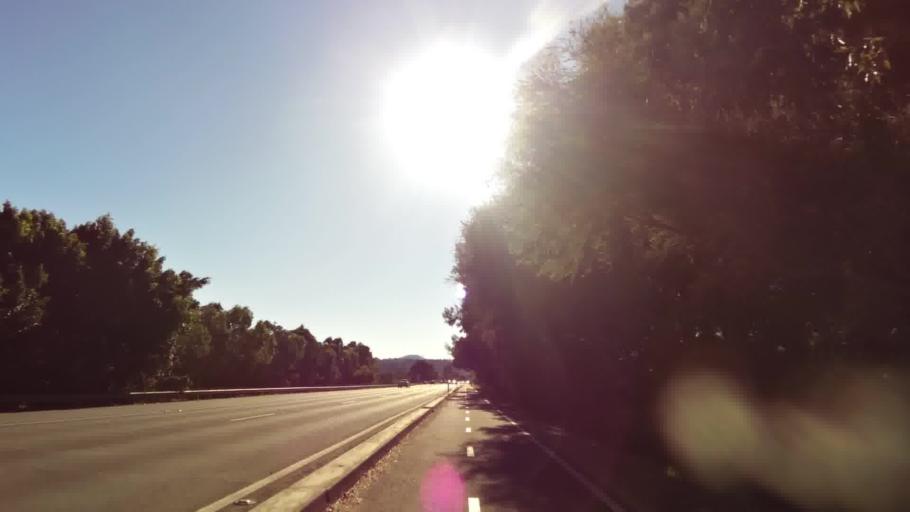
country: AU
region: New South Wales
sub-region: Wollongong
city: Koonawarra
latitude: -34.4852
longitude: 150.8006
